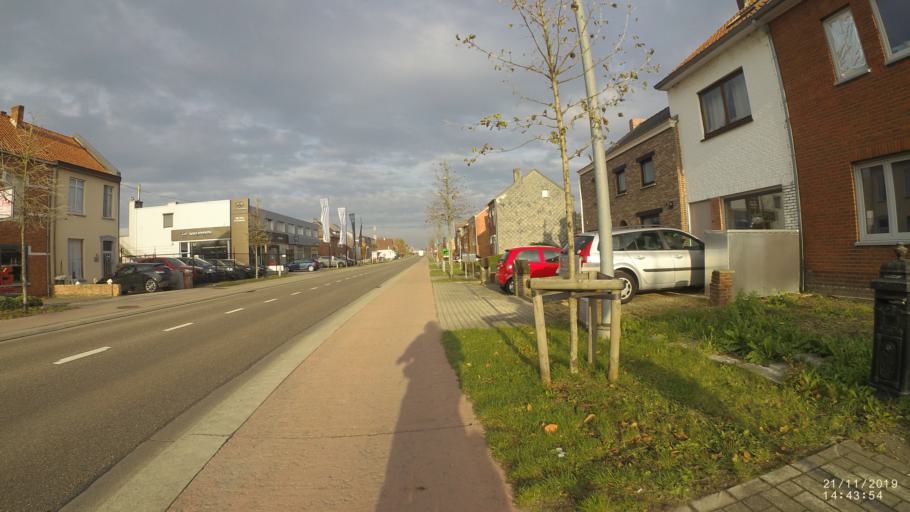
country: BE
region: Flanders
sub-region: Provincie Limburg
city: Hasselt
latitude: 50.9088
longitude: 5.3180
